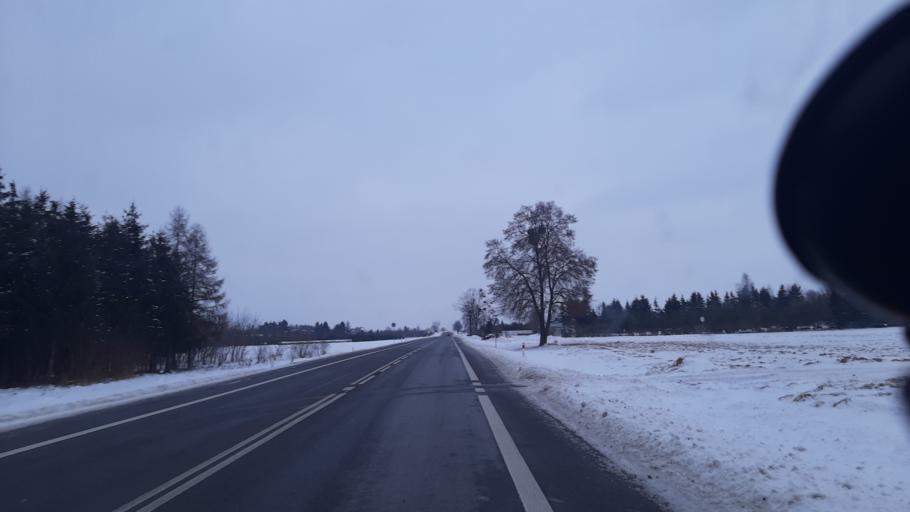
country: PL
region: Lublin Voivodeship
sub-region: Powiat pulawski
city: Kurow
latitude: 51.3849
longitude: 22.2136
